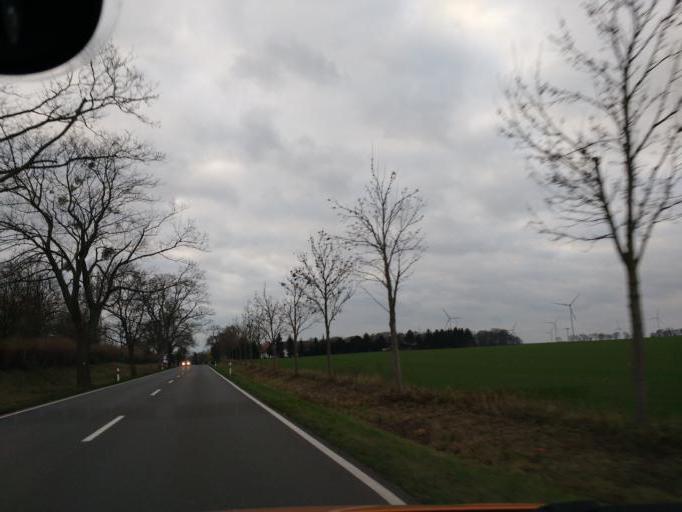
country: DE
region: Brandenburg
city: Wriezen
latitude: 52.6931
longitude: 14.1054
